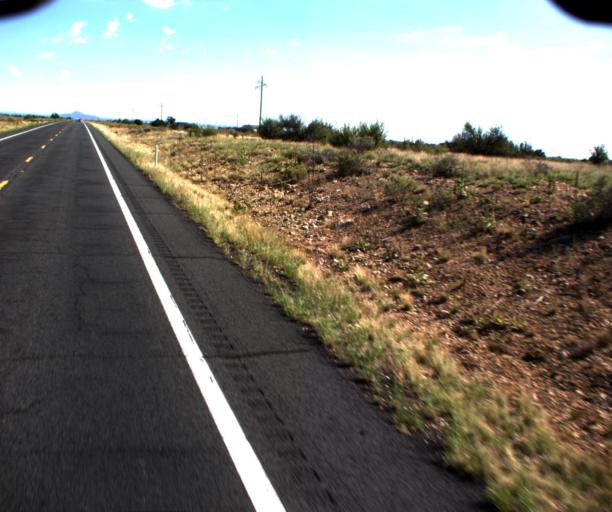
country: US
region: Arizona
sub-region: Coconino County
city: Williams
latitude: 35.5892
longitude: -112.1501
